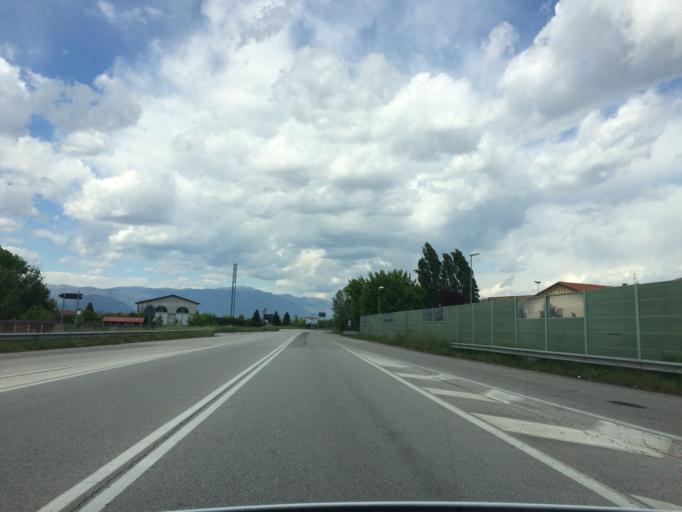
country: IT
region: Veneto
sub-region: Provincia di Padova
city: Cittadella
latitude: 45.6497
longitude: 11.7741
